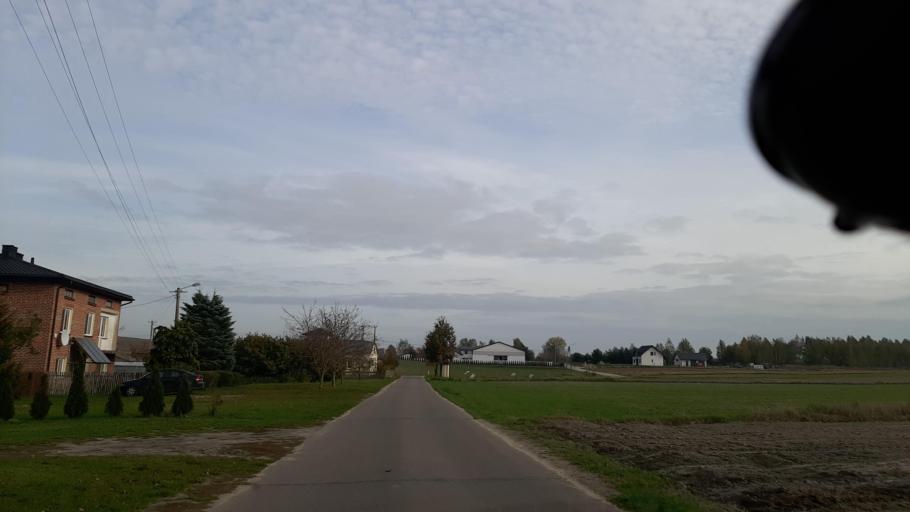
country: PL
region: Lublin Voivodeship
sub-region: Powiat lubelski
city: Garbow
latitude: 51.4094
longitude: 22.3901
